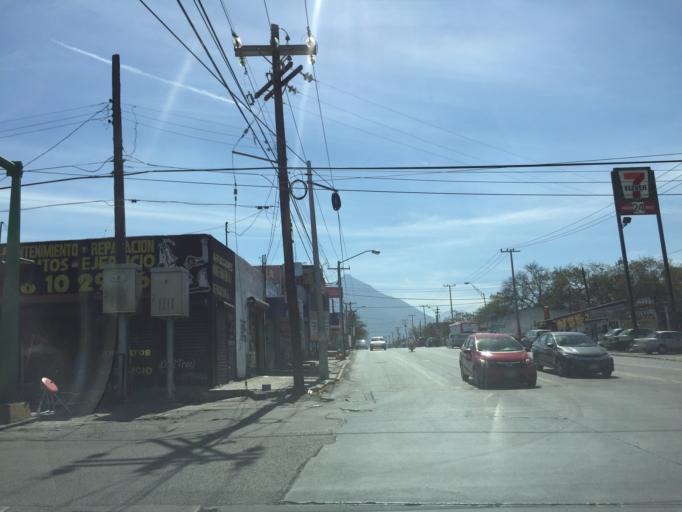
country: MX
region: Nuevo Leon
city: Guadalupe
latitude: 25.7030
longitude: -100.2466
